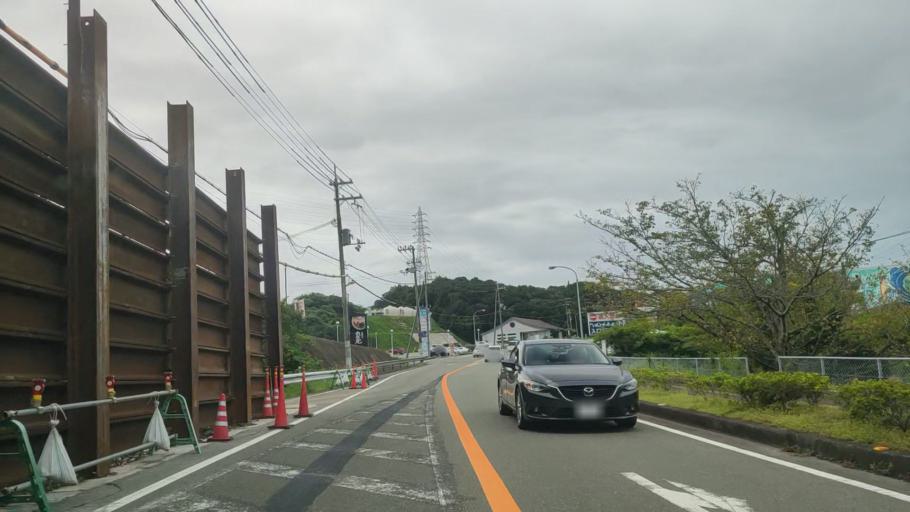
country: JP
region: Wakayama
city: Tanabe
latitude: 33.6819
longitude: 135.3776
